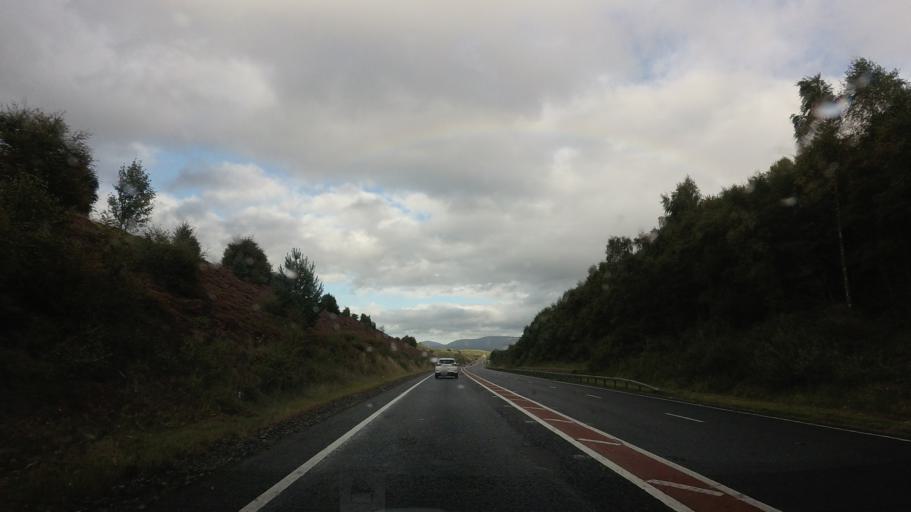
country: GB
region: Scotland
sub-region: Highland
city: Kingussie
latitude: 57.0569
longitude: -4.1031
